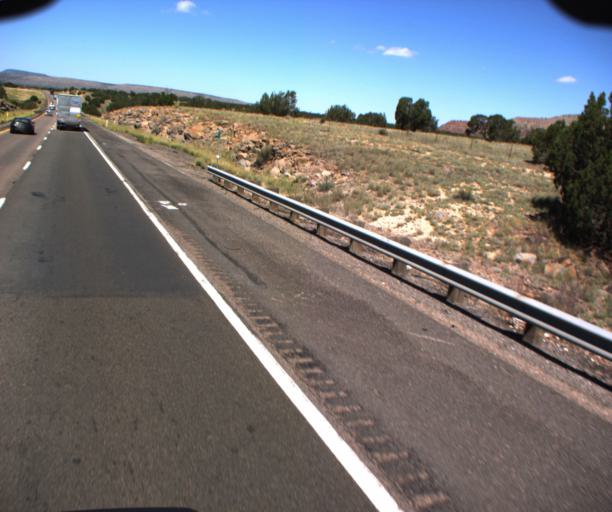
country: US
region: Arizona
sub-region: Mohave County
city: Peach Springs
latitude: 35.3231
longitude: -112.9194
